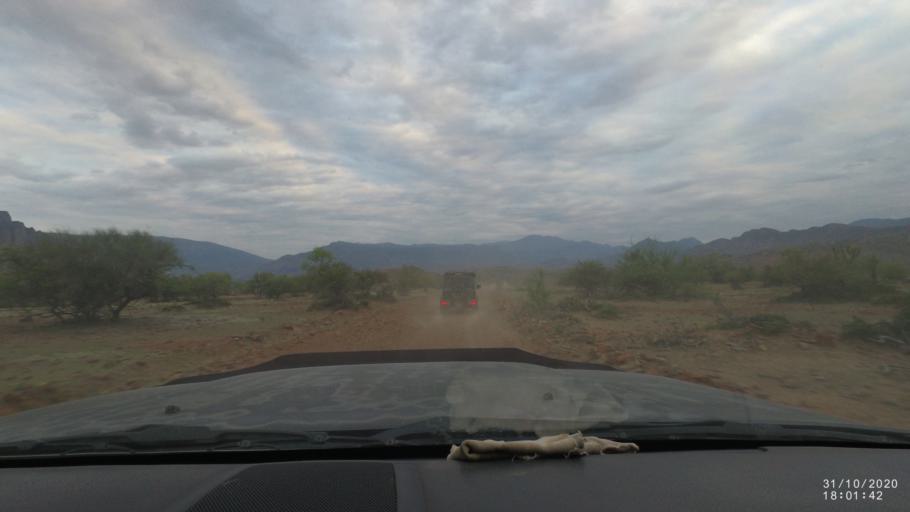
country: BO
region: Chuquisaca
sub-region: Provincia Zudanez
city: Mojocoya
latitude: -18.6641
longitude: -64.5300
